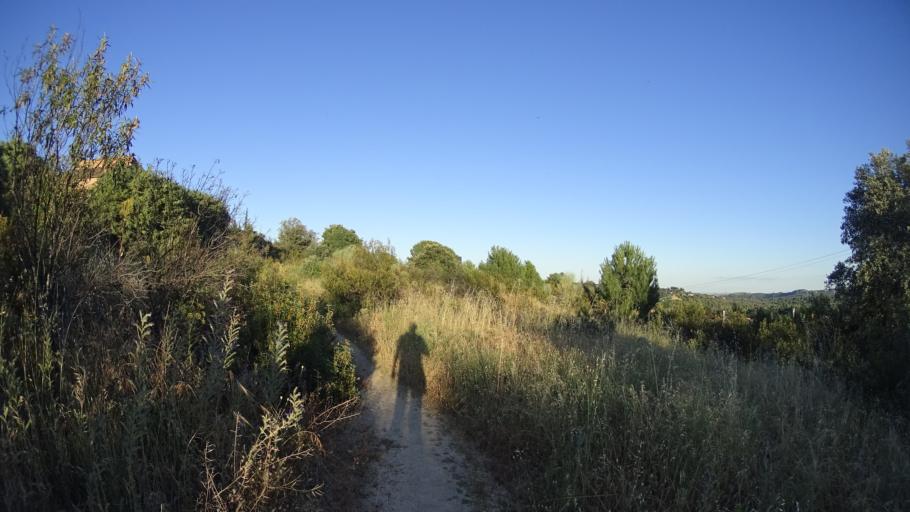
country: ES
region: Madrid
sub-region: Provincia de Madrid
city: Galapagar
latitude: 40.5906
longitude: -3.9699
